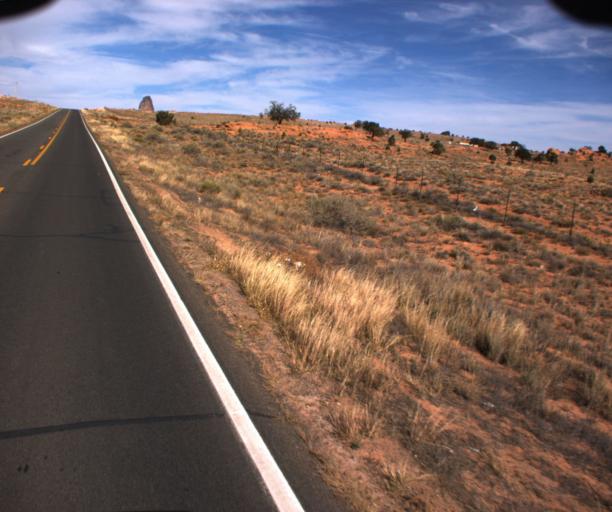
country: US
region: Arizona
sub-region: Navajo County
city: Kayenta
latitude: 36.7524
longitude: -110.2259
